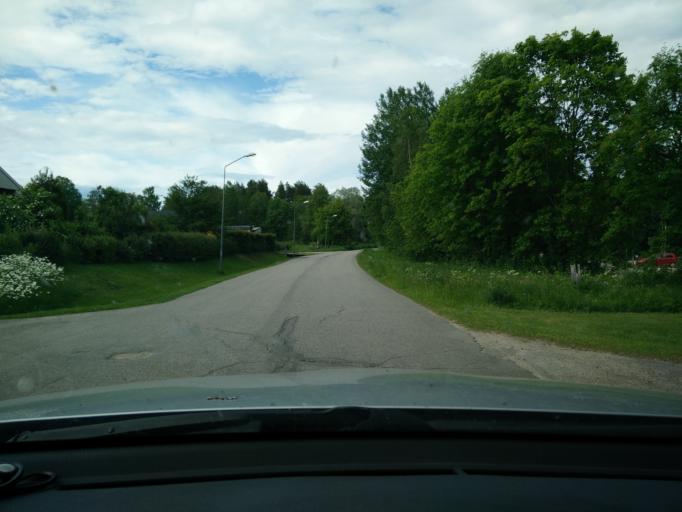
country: SE
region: Gaevleborg
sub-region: Nordanstigs Kommun
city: Bergsjoe
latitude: 61.9776
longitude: 17.0524
